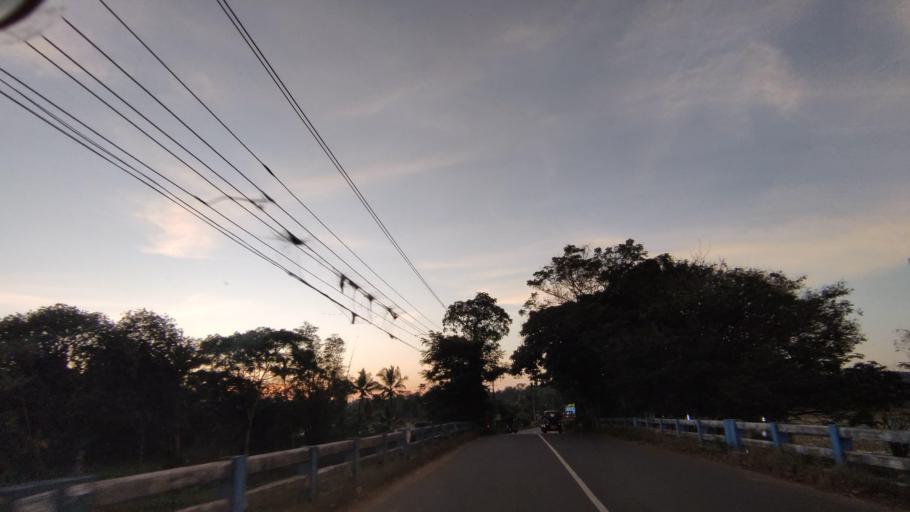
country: IN
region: Kerala
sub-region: Kottayam
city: Kottayam
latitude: 9.6925
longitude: 76.4912
